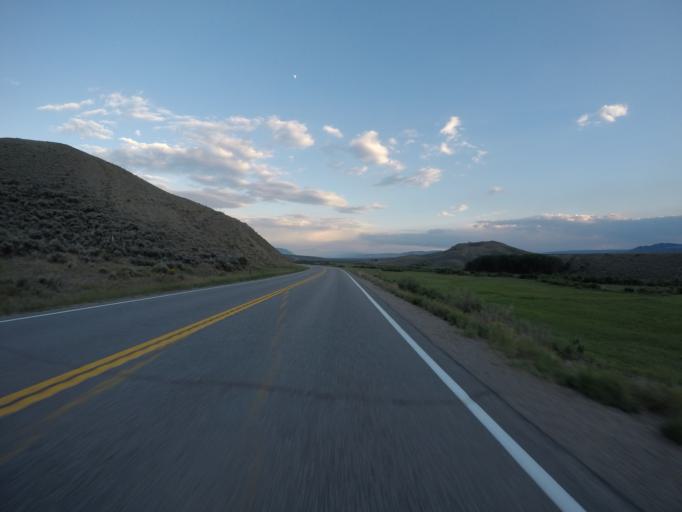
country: US
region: Colorado
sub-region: Grand County
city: Kremmling
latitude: 40.2380
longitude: -106.4396
